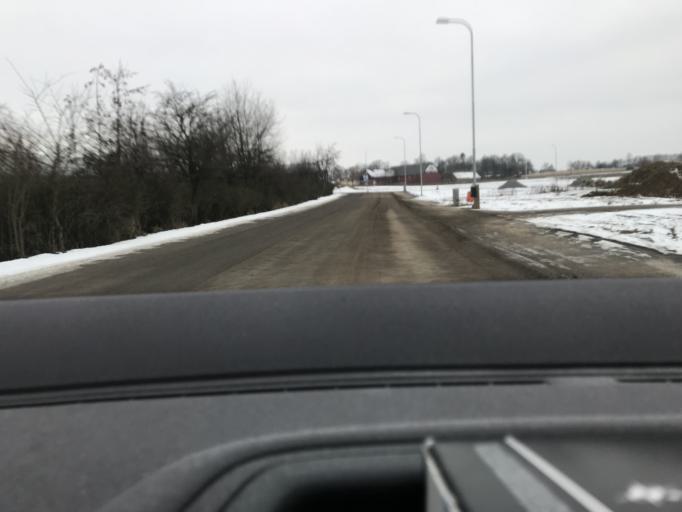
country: SE
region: Skane
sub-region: Ystads Kommun
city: Ystad
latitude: 55.4507
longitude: 13.8518
